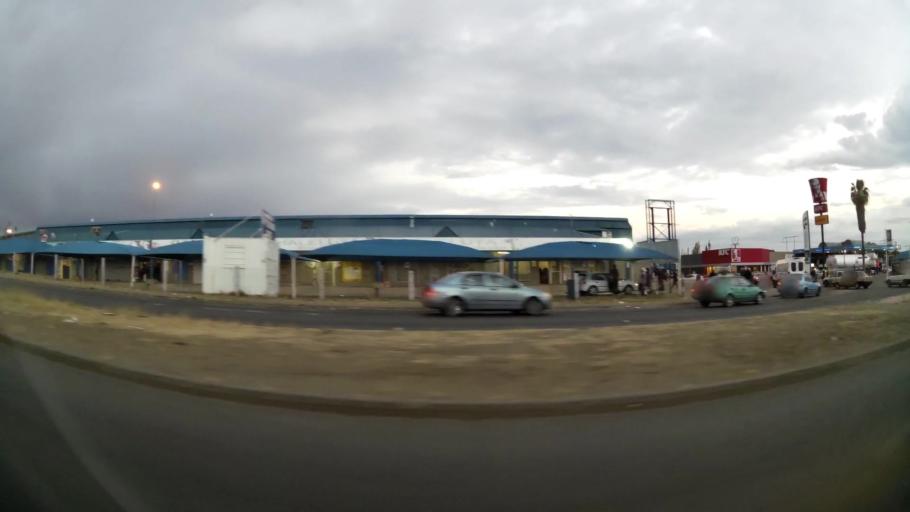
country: ZA
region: Orange Free State
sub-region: Lejweleputswa District Municipality
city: Welkom
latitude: -27.9793
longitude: 26.7739
